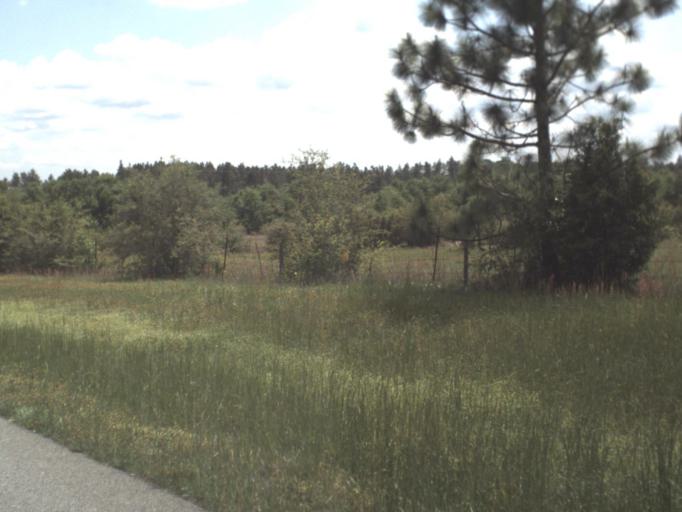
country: US
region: Florida
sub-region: Escambia County
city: Molino
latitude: 30.8123
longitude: -87.4270
